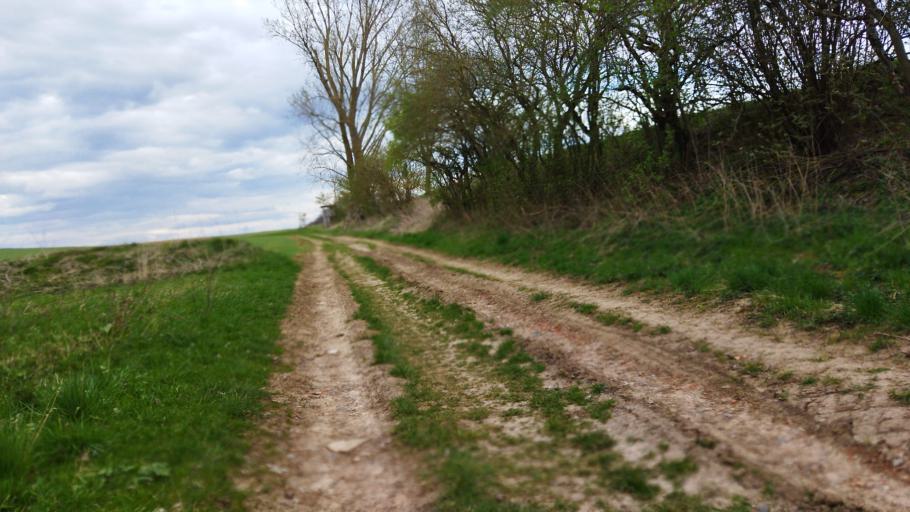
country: DE
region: Baden-Wuerttemberg
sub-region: Regierungsbezirk Stuttgart
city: Oedheim
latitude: 49.2194
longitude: 9.2808
